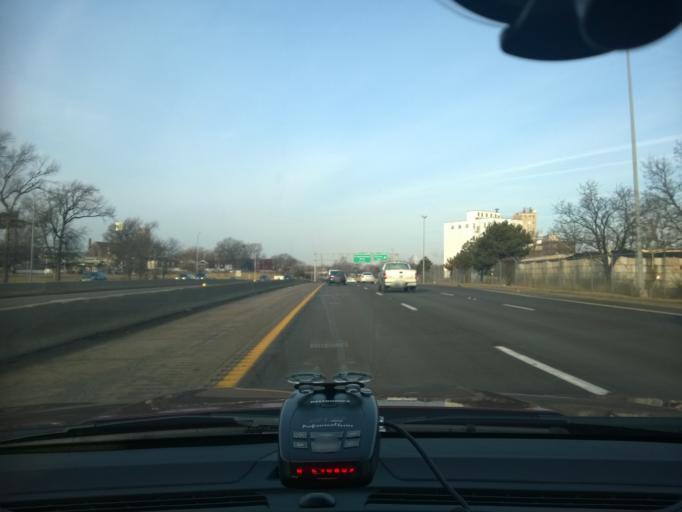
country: US
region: Missouri
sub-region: Saint Louis County
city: Pine Lawn
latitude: 38.6830
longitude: -90.2352
